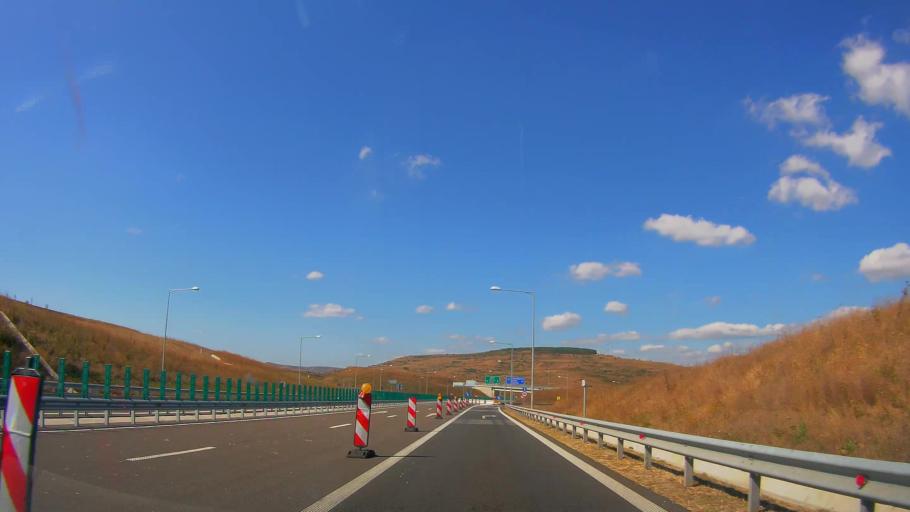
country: RO
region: Cluj
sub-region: Comuna Baciu
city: Mera
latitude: 46.8072
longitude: 23.4234
